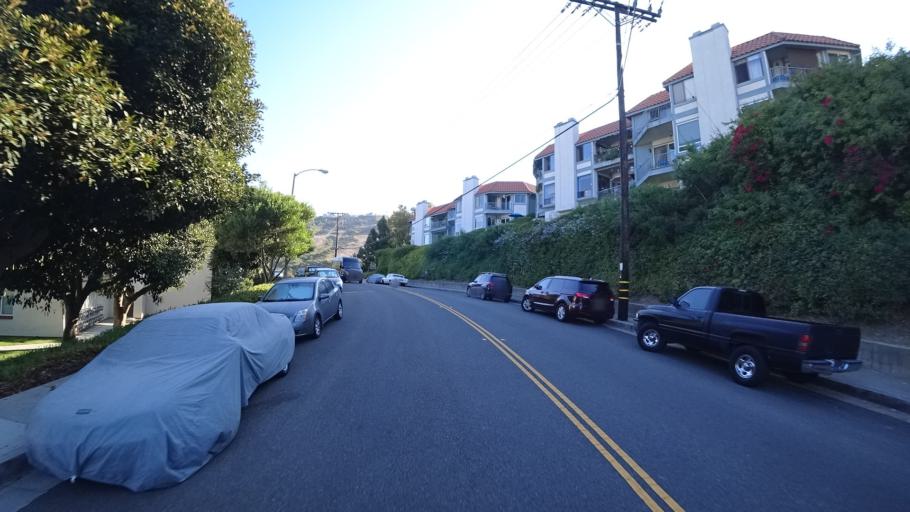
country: US
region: California
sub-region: Orange County
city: San Clemente
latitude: 33.4284
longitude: -117.6079
